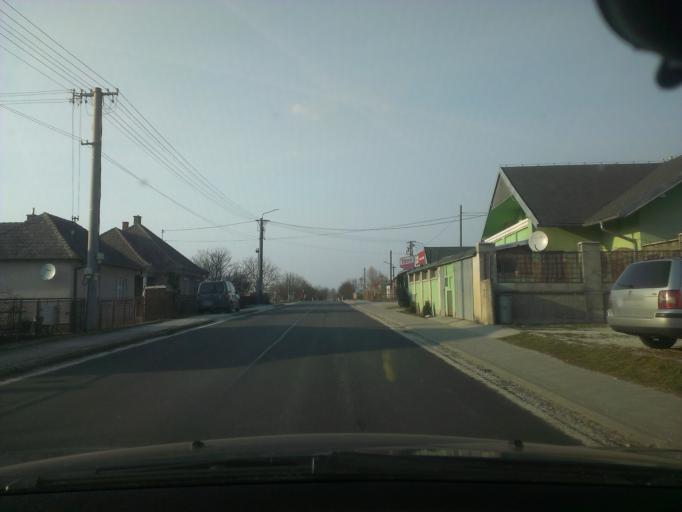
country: SK
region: Trnavsky
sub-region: Okres Trnava
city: Piestany
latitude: 48.6585
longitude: 17.8781
